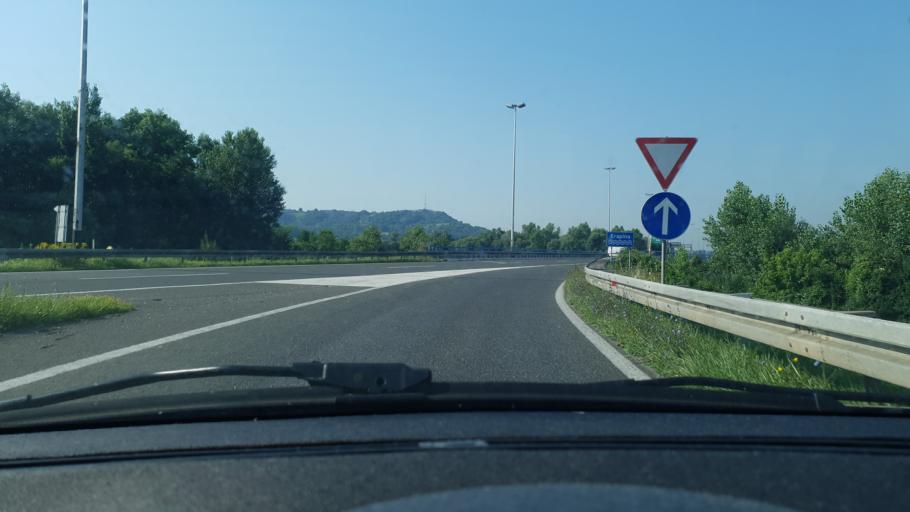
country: HR
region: Zagrebacka
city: Zapresic
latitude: 45.8514
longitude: 15.8255
